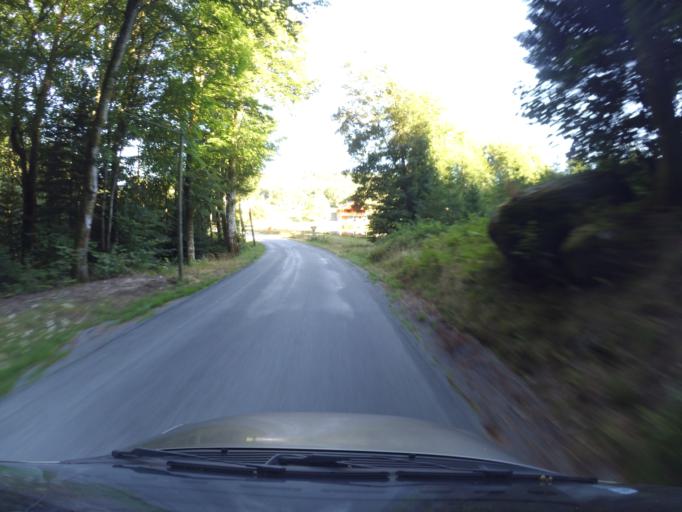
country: FR
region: Limousin
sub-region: Departement de la Creuse
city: Banize
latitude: 45.7829
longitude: 1.9893
